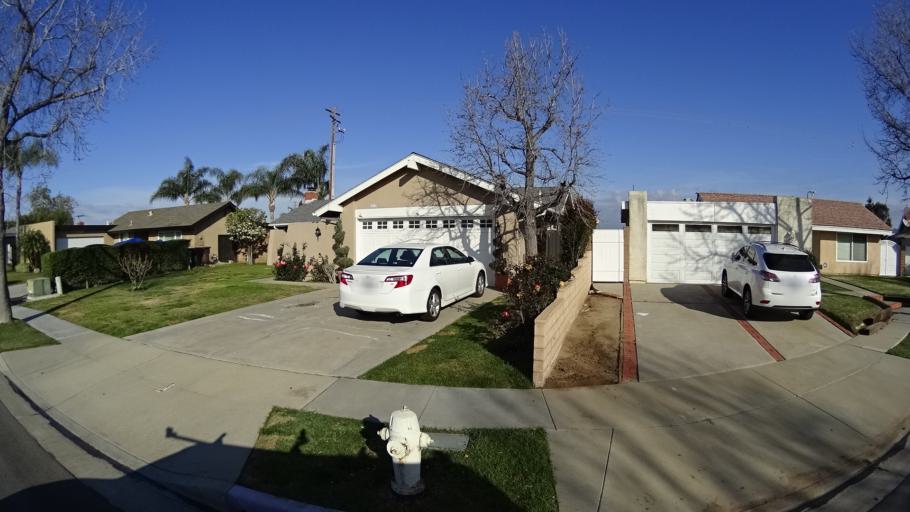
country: US
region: California
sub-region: Orange County
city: Yorba Linda
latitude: 33.8525
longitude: -117.8227
